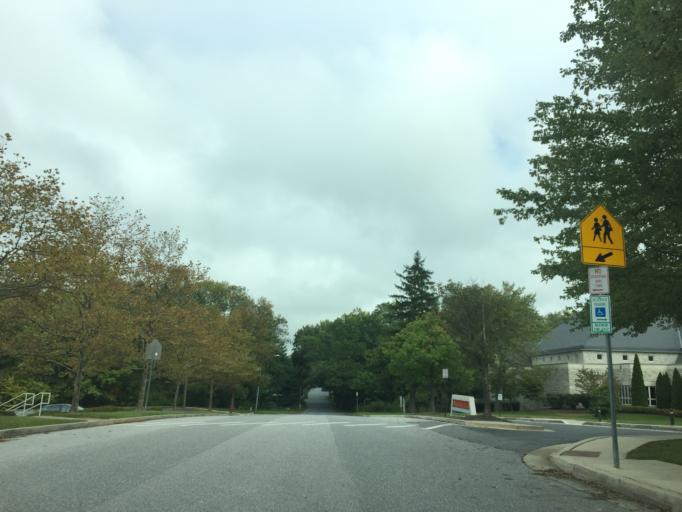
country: US
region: Maryland
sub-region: Baltimore County
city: Reisterstown
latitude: 39.4704
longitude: -76.8219
